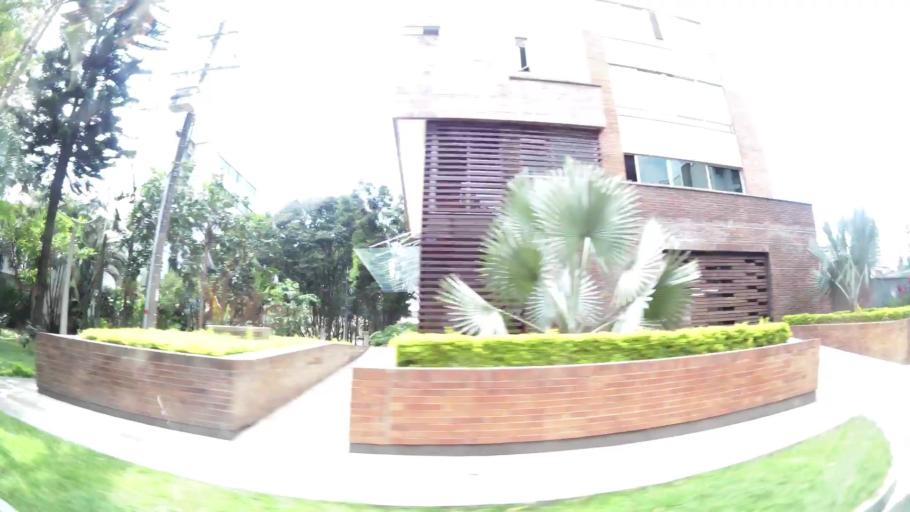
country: CO
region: Antioquia
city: Envigado
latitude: 6.1861
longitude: -75.5815
